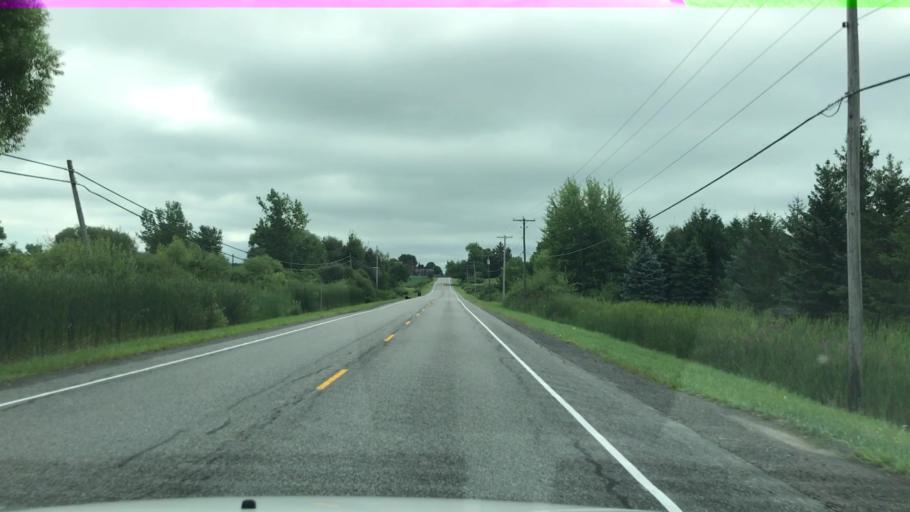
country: US
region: New York
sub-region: Wyoming County
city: Attica
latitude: 42.8361
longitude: -78.3600
